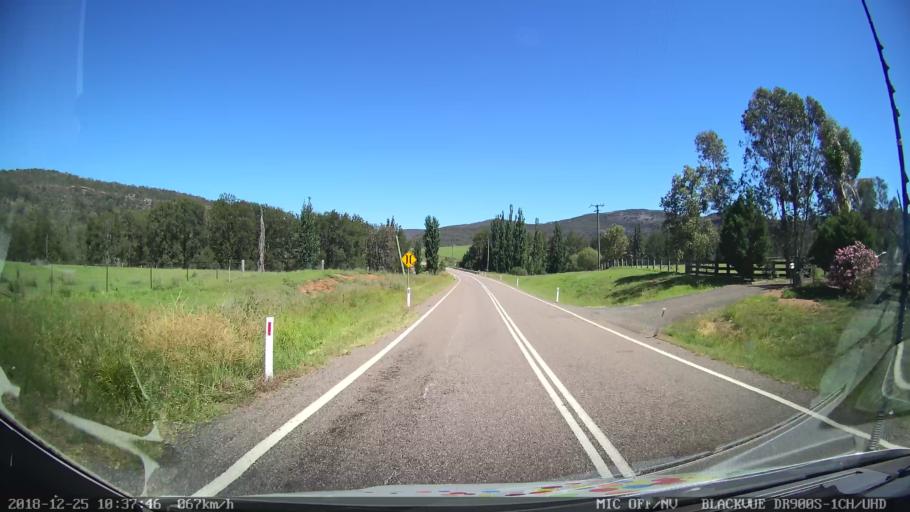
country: AU
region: New South Wales
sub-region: Upper Hunter Shire
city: Merriwa
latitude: -32.4073
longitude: 150.3750
